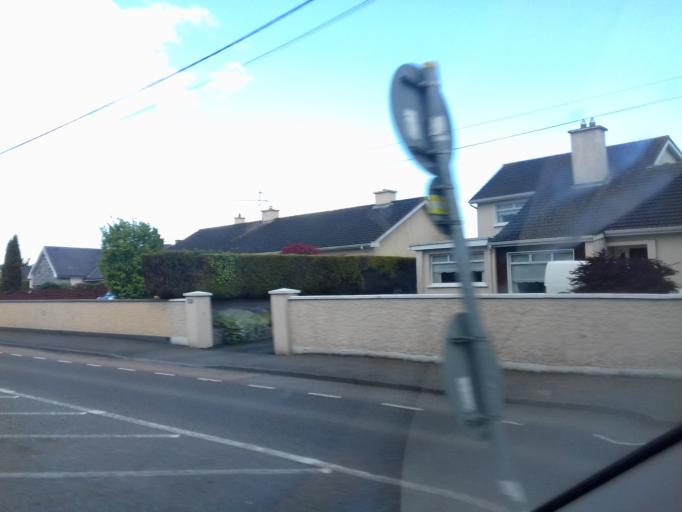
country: IE
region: Leinster
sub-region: Kilkenny
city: Kilkenny
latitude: 52.6390
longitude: -7.2494
